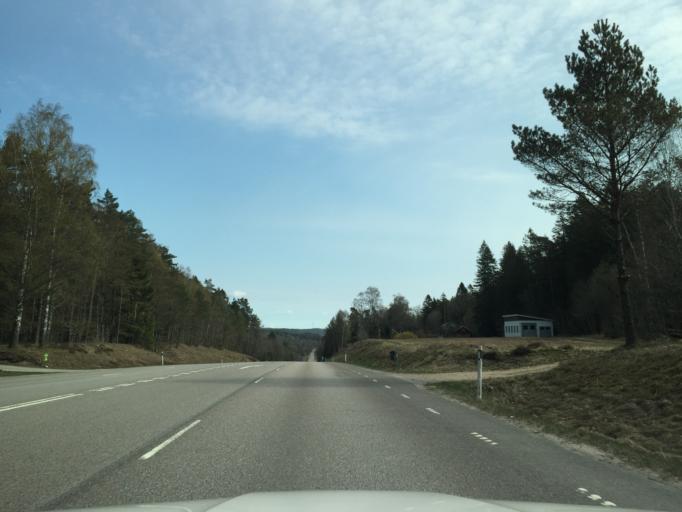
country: SE
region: Vaestra Goetaland
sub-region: Stenungsunds Kommun
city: Stora Hoga
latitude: 58.0564
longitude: 11.9111
